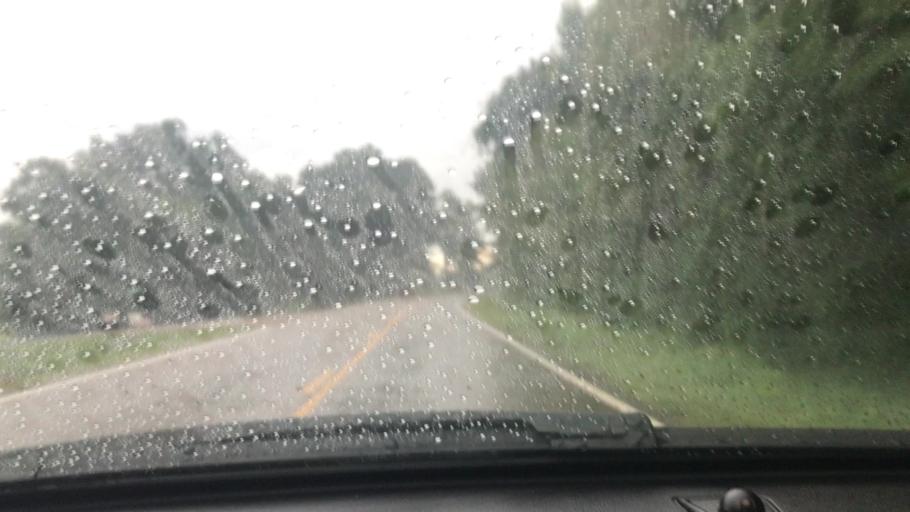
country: US
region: Mississippi
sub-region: Pike County
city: Summit
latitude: 31.3174
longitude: -90.5286
